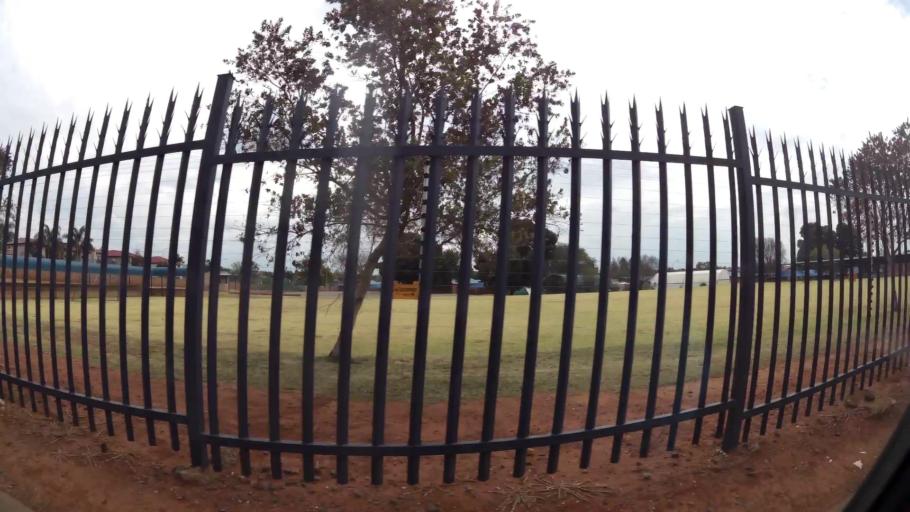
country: ZA
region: Gauteng
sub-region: City of Johannesburg Metropolitan Municipality
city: Roodepoort
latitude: -26.0943
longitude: 27.8769
